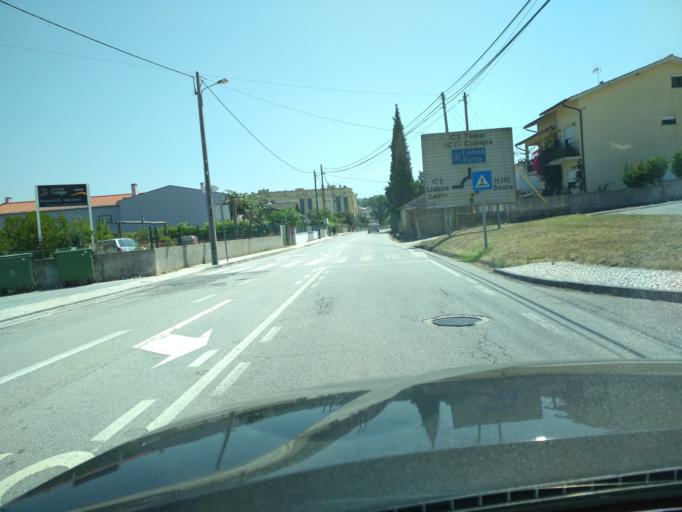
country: PT
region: Coimbra
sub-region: Condeixa-A-Nova
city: Condeixa-a-Nova
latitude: 40.1096
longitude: -8.5068
